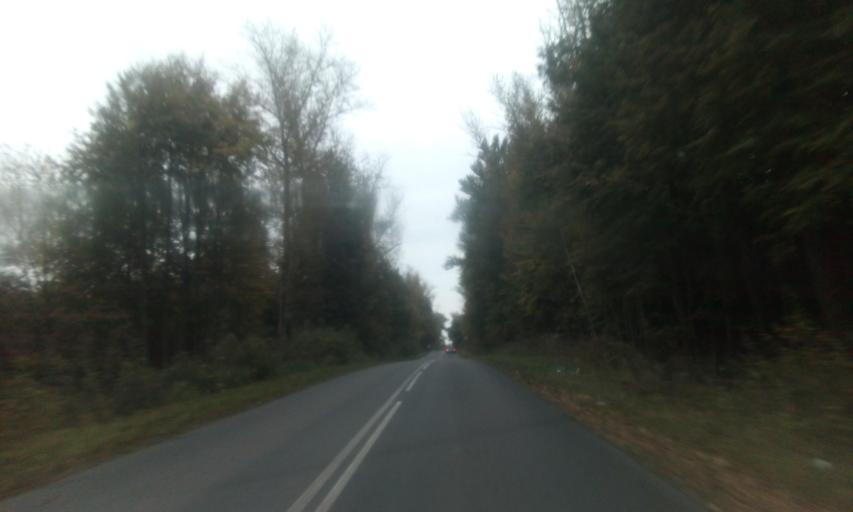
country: RU
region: Tula
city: Partizan
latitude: 53.9618
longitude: 38.0872
